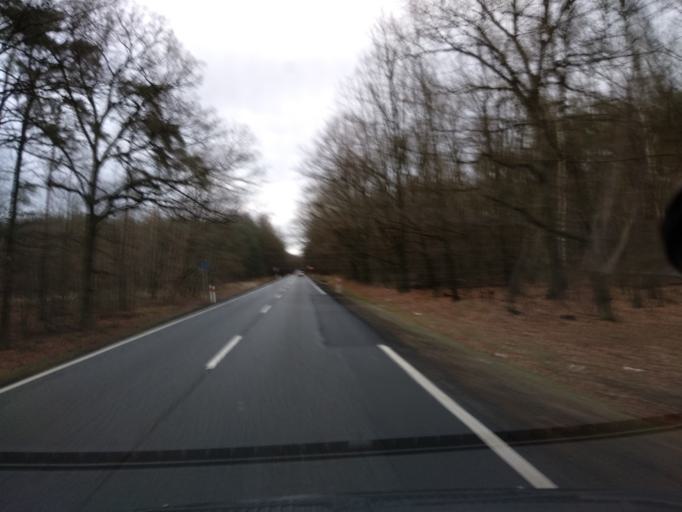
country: PL
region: Lower Silesian Voivodeship
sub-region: Powiat olesnicki
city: Olesnica
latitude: 51.2366
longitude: 17.4552
